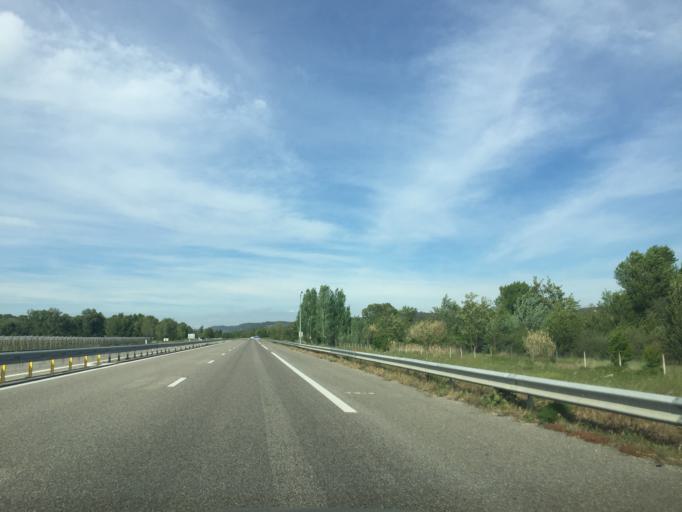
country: FR
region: Provence-Alpes-Cote d'Azur
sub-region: Departement des Alpes-de-Haute-Provence
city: Manosque
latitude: 43.8209
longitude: 5.8309
